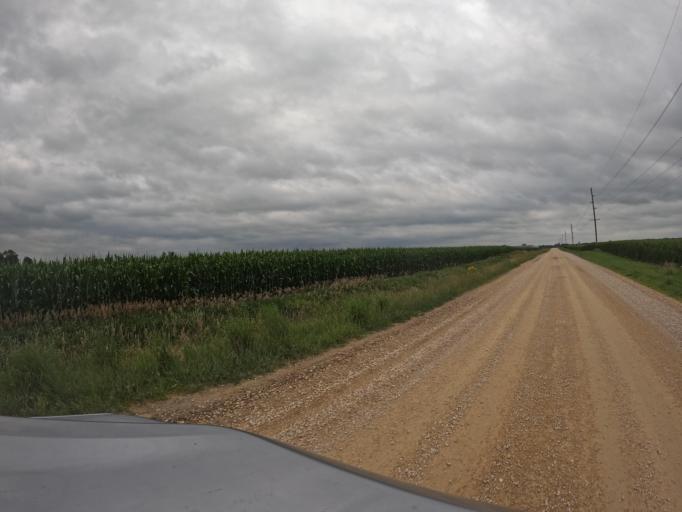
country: US
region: Iowa
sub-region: Clinton County
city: De Witt
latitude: 41.7999
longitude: -90.4714
